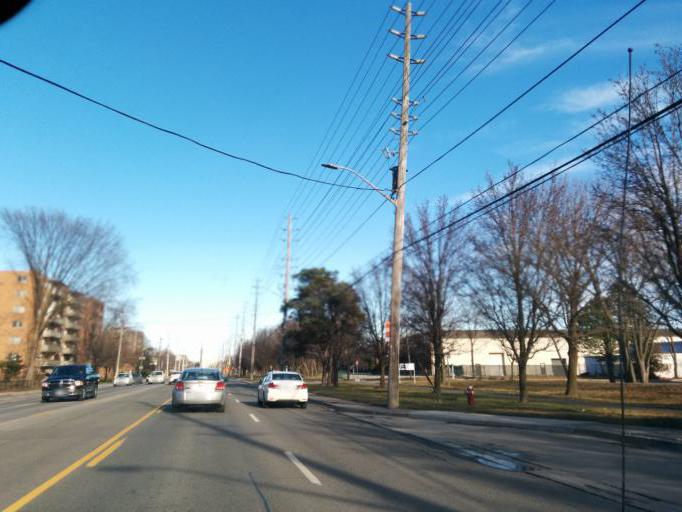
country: CA
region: Ontario
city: Etobicoke
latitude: 43.5814
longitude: -79.5541
